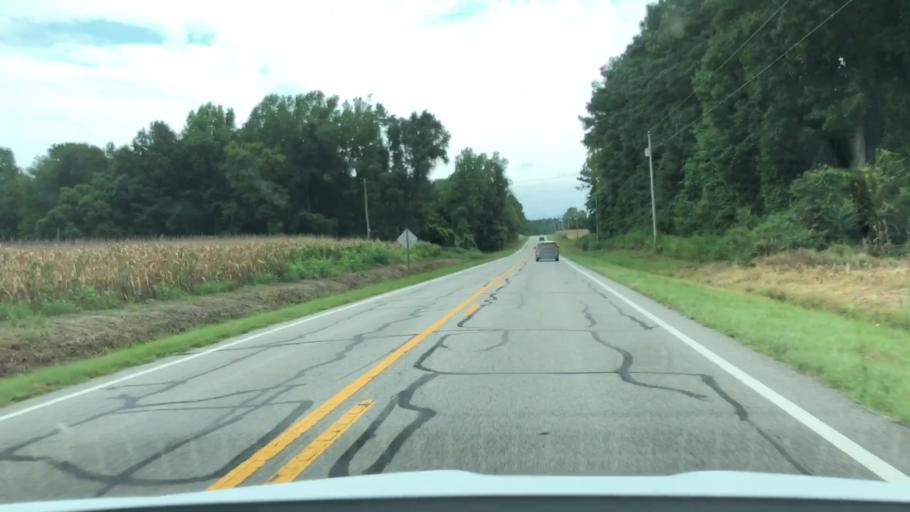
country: US
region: North Carolina
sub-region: Lenoir County
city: Kinston
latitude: 35.1659
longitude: -77.5570
